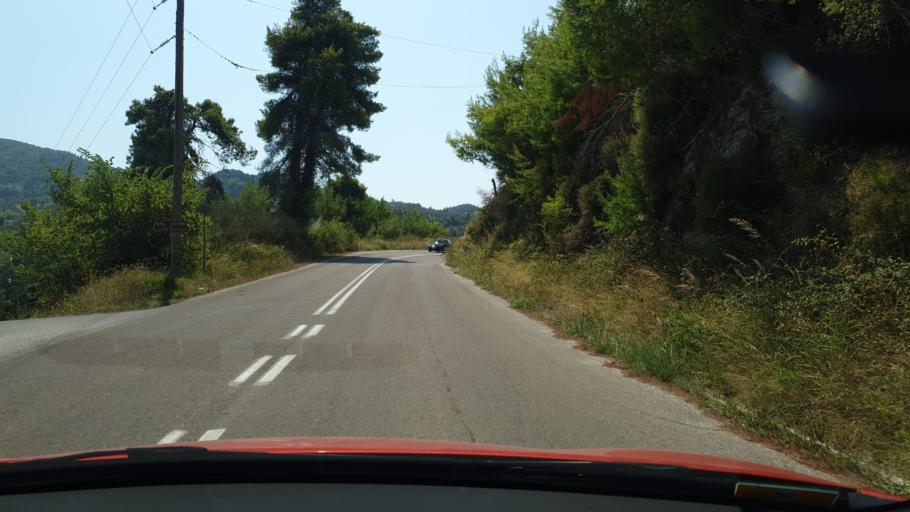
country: GR
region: Central Greece
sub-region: Nomos Evvoias
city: Oxilithos
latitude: 38.5961
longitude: 24.0753
